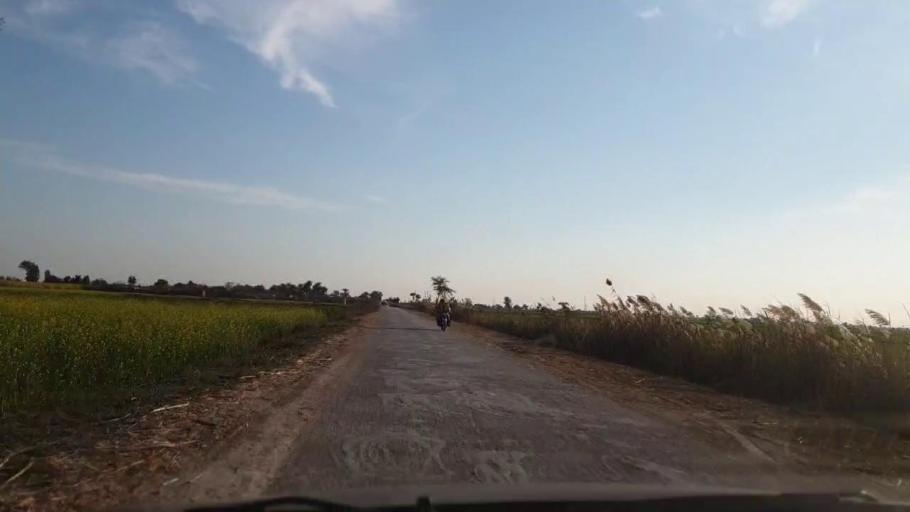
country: PK
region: Sindh
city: Khadro
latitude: 26.1754
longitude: 68.7529
